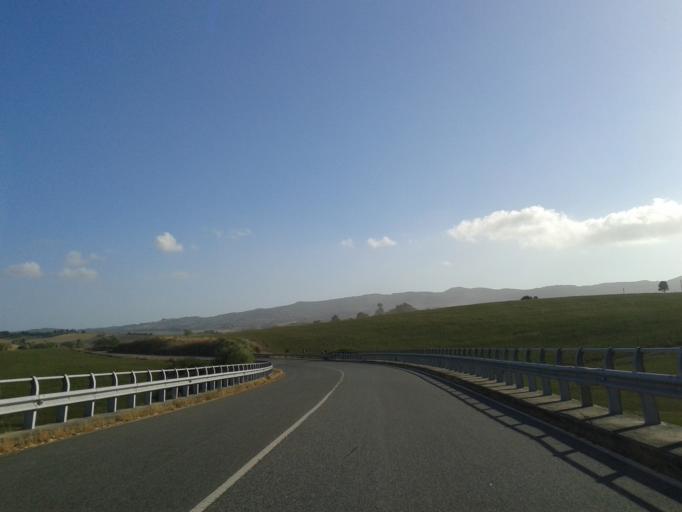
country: IT
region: Tuscany
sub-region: Province of Pisa
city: Castellina Marittima
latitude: 43.4212
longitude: 10.5860
